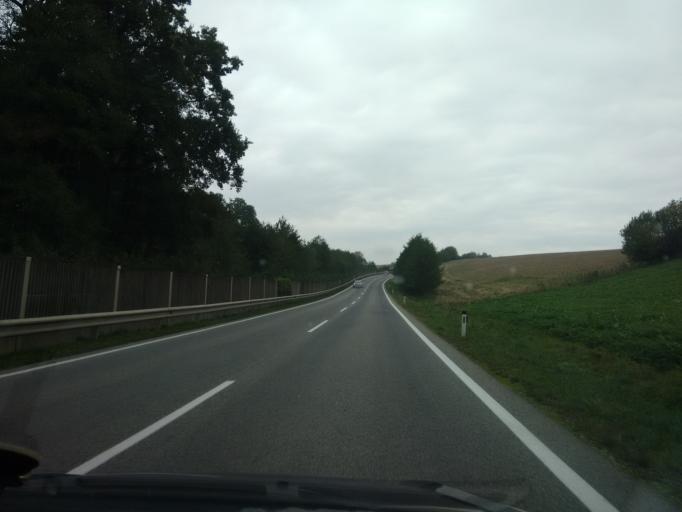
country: AT
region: Upper Austria
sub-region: Politischer Bezirk Steyr-Land
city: Bad Hall
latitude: 48.0617
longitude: 14.1876
